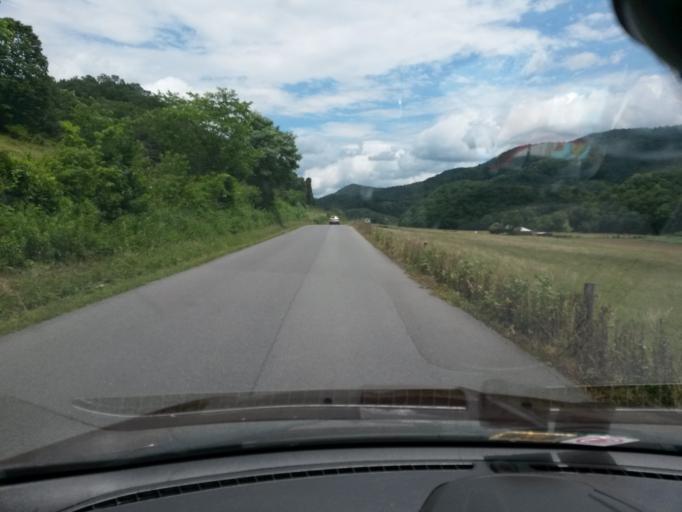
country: US
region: West Virginia
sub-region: Monroe County
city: Union
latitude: 37.5006
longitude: -80.5947
